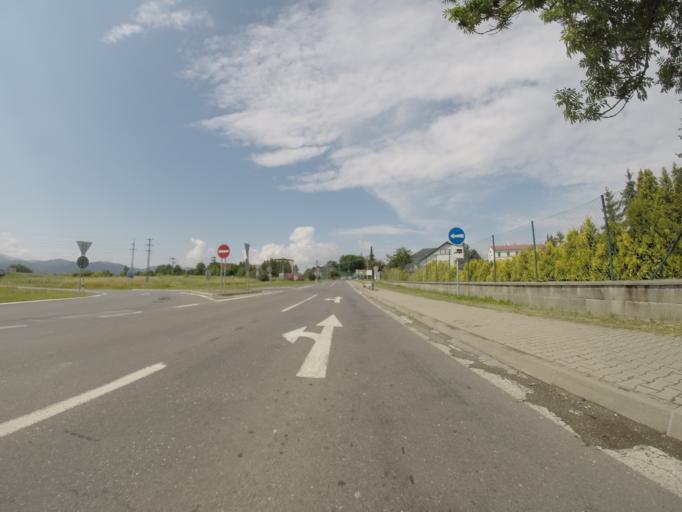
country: SK
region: Banskobystricky
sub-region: Okres Banska Bystrica
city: Zvolen
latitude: 48.6009
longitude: 19.1069
